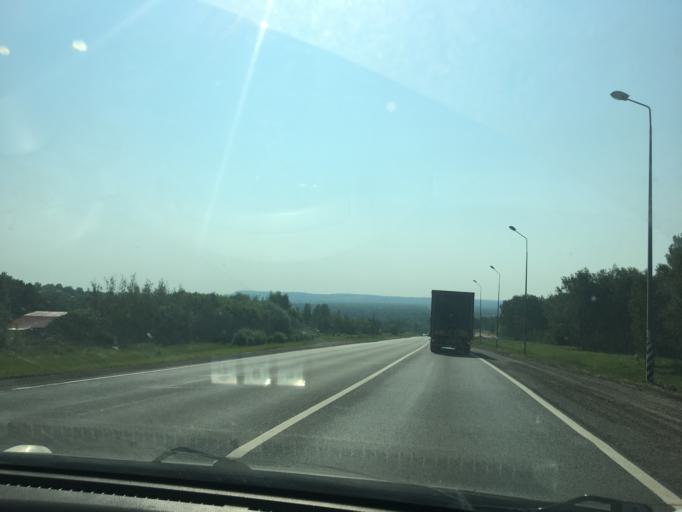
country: RU
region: Nizjnij Novgorod
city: Kstovo
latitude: 56.1050
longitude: 44.2916
